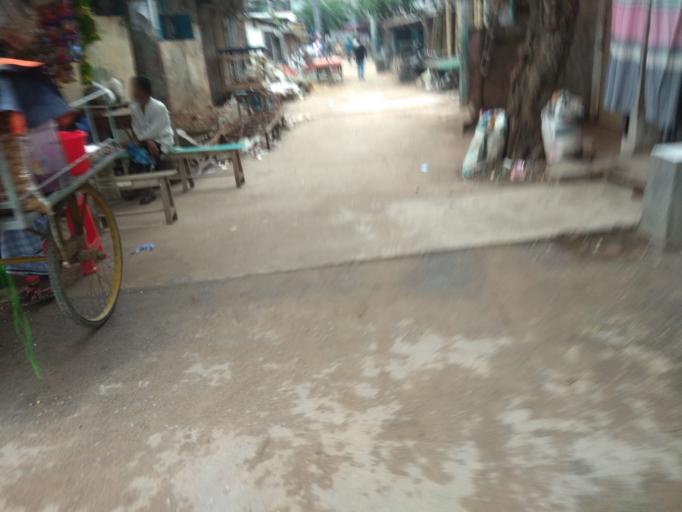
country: BD
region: Dhaka
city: Tungi
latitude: 23.8263
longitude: 90.3762
